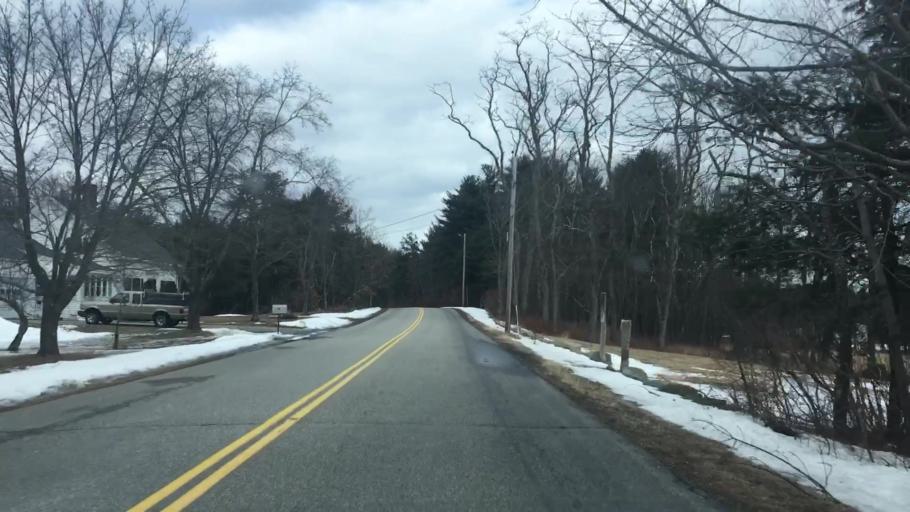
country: US
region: Maine
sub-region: York County
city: Wells Beach Station
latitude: 43.3106
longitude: -70.6537
